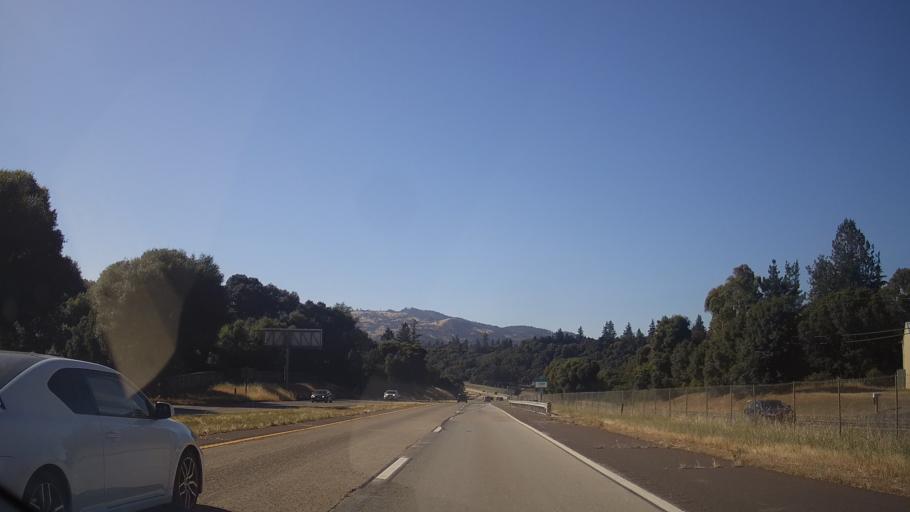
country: US
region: California
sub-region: Mendocino County
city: Redwood Valley
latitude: 39.2489
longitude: -123.2101
